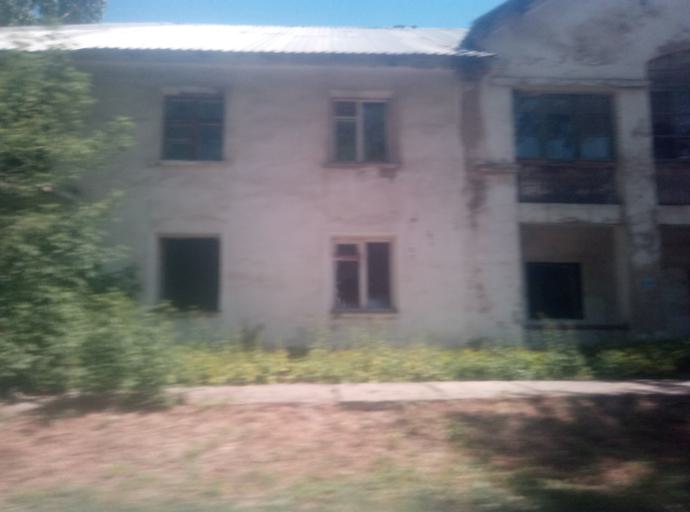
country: RU
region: Tula
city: Kireyevsk
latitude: 53.9272
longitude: 37.9218
